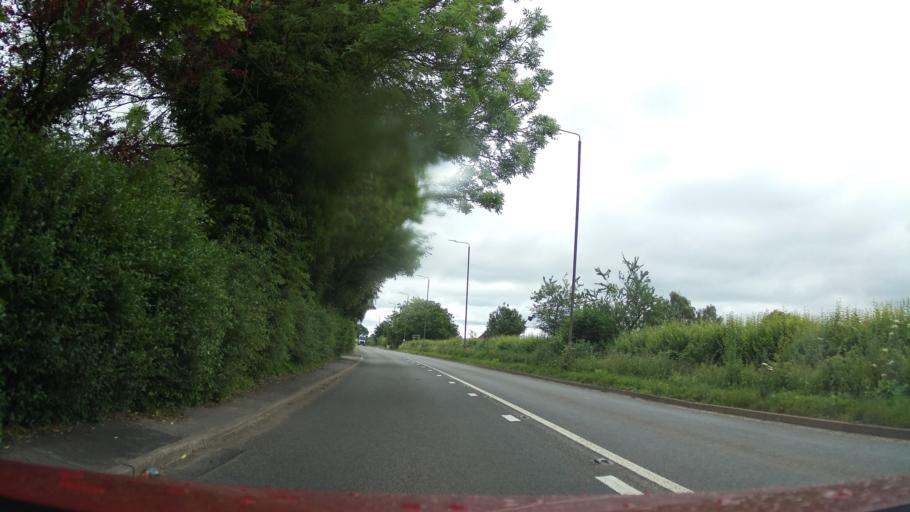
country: GB
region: England
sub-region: Derbyshire
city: Rodsley
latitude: 52.8756
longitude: -1.6929
